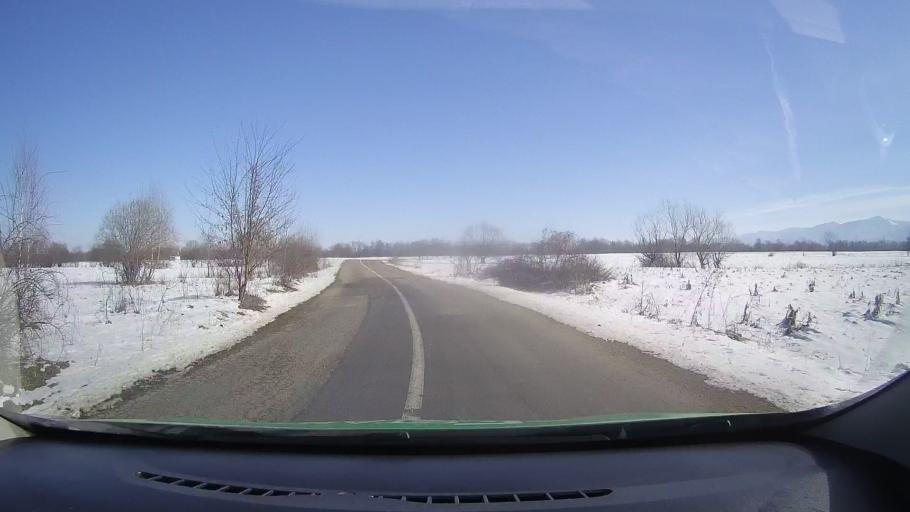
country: RO
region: Brasov
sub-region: Comuna Recea
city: Recea
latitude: 45.7291
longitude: 24.9724
